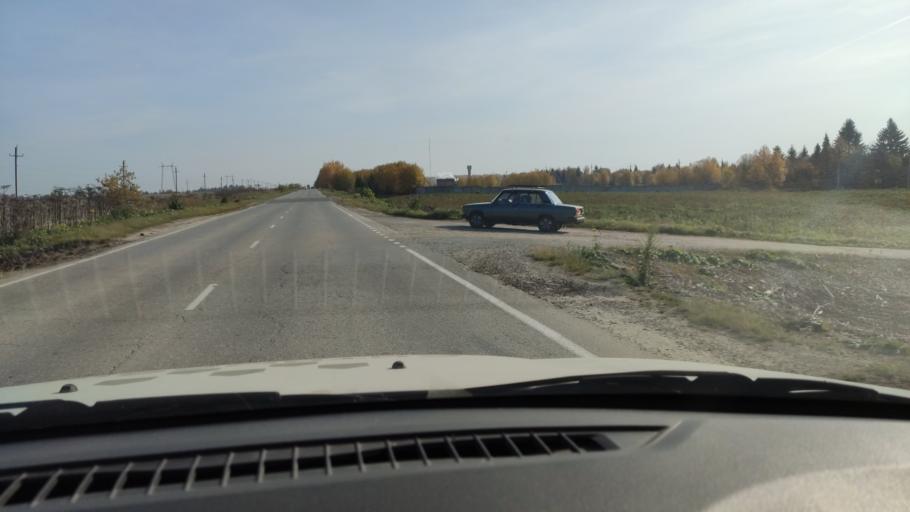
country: RU
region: Perm
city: Sylva
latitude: 58.0295
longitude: 56.6990
